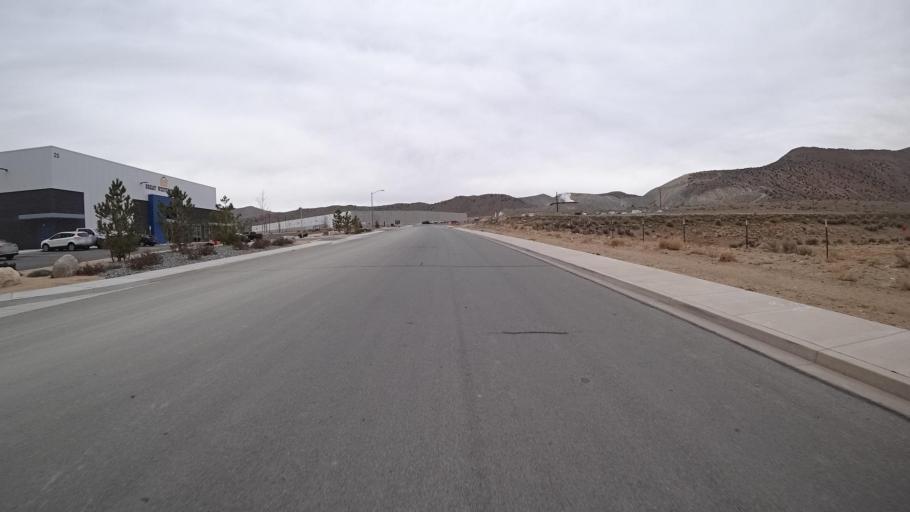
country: US
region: Nevada
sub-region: Washoe County
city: Spanish Springs
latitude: 39.6771
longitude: -119.7165
